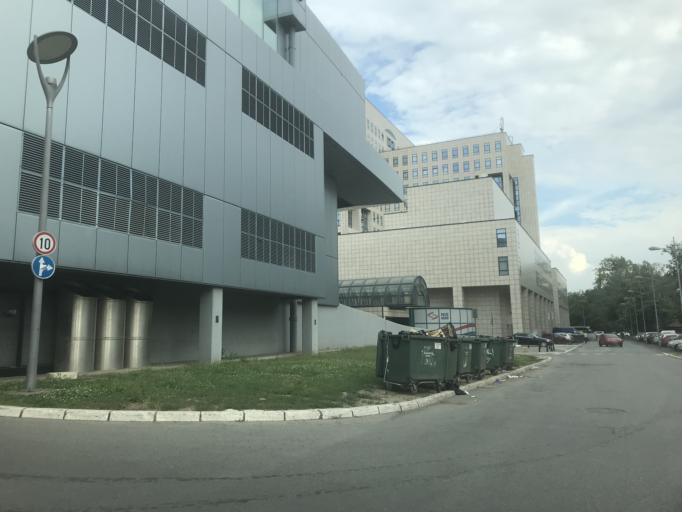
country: RS
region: Autonomna Pokrajina Vojvodina
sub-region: Juznobacki Okrug
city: Novi Sad
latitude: 45.2428
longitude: 19.8398
